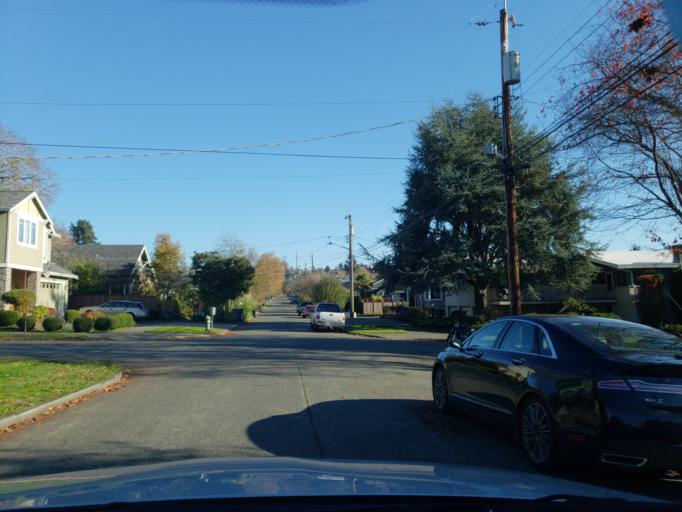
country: US
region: Washington
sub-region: King County
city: Seattle
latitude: 47.6738
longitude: -122.3717
